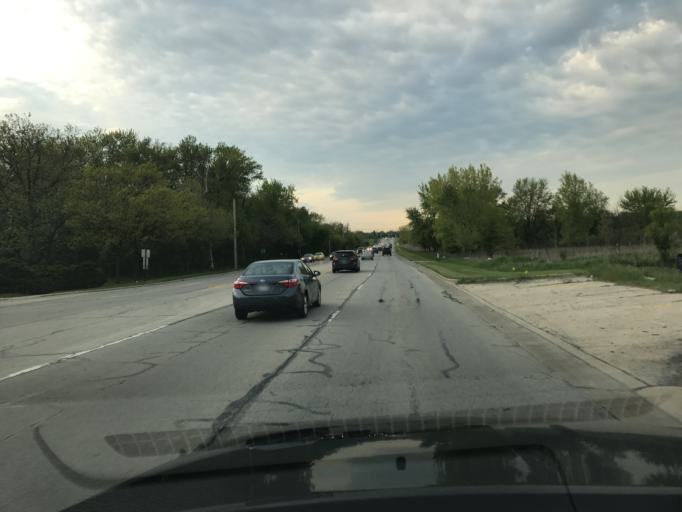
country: US
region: Illinois
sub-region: Will County
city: Bolingbrook
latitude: 41.7066
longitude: -88.1267
